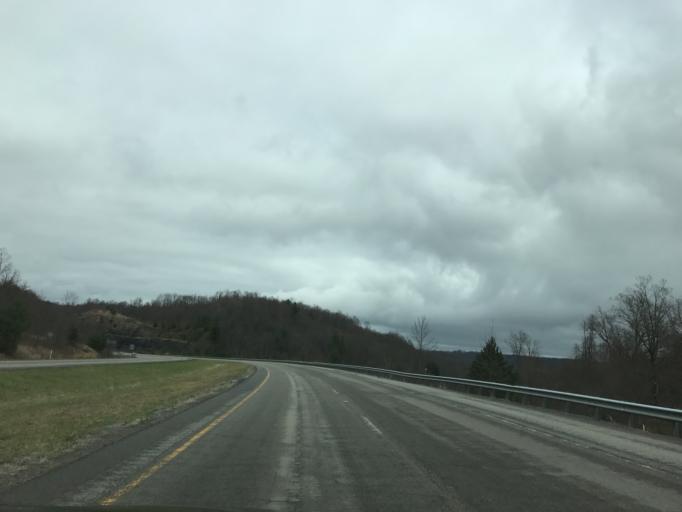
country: US
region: West Virginia
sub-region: Raleigh County
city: Sophia
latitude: 37.7125
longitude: -81.2619
